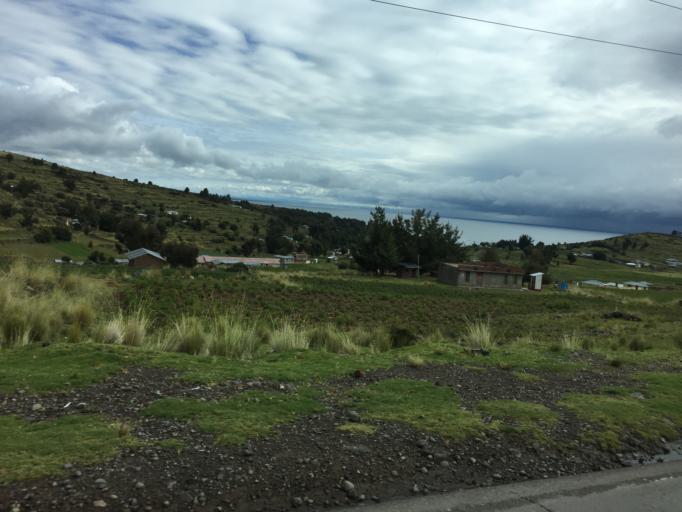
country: PE
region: Puno
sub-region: Provincia de Chucuito
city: Juli
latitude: -16.2025
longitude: -69.4215
